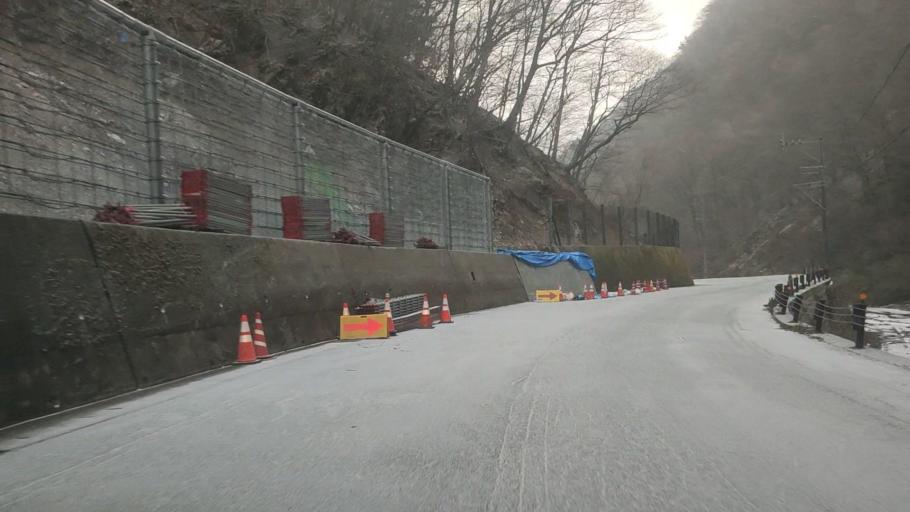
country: JP
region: Kumamoto
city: Matsubase
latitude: 32.5551
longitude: 130.9247
